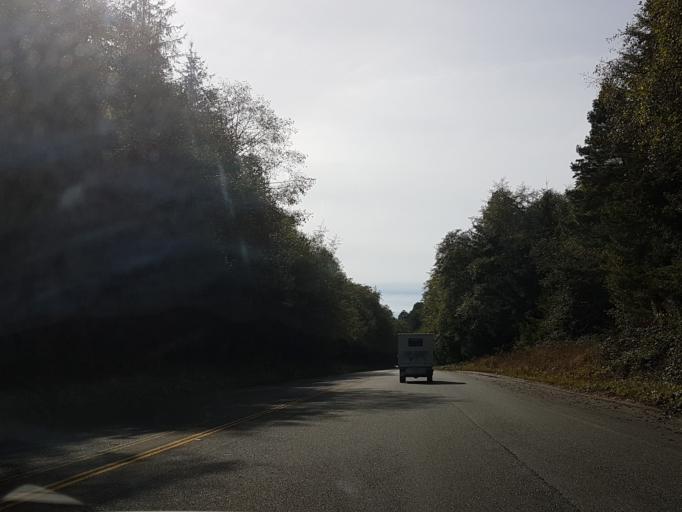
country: US
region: California
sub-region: Del Norte County
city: Bertsch-Oceanview
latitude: 41.4647
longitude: -124.0420
